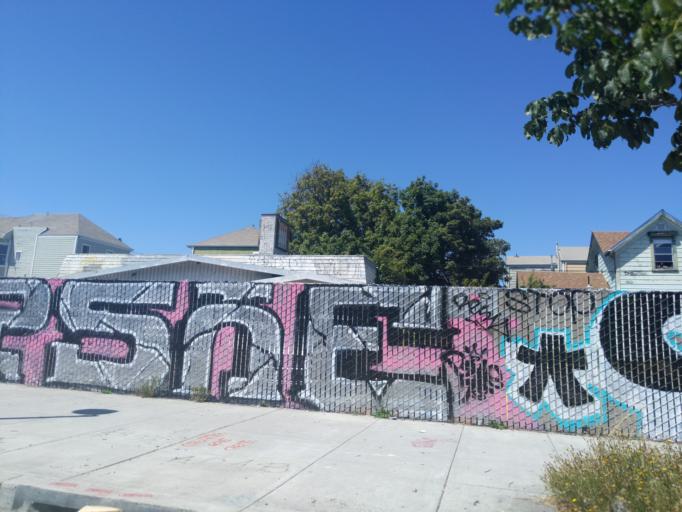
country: US
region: California
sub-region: Alameda County
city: Oakland
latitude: 37.8057
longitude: -122.2963
